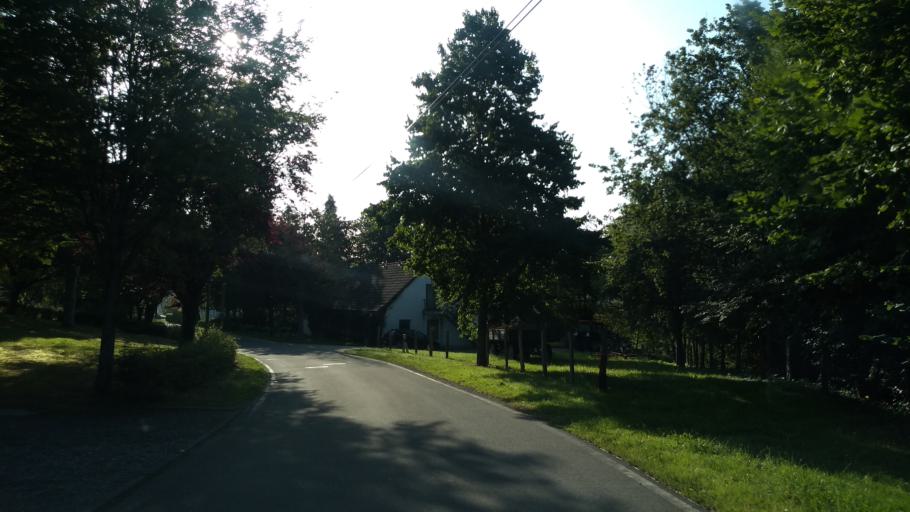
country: DE
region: North Rhine-Westphalia
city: Wiehl
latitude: 50.9422
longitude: 7.5060
